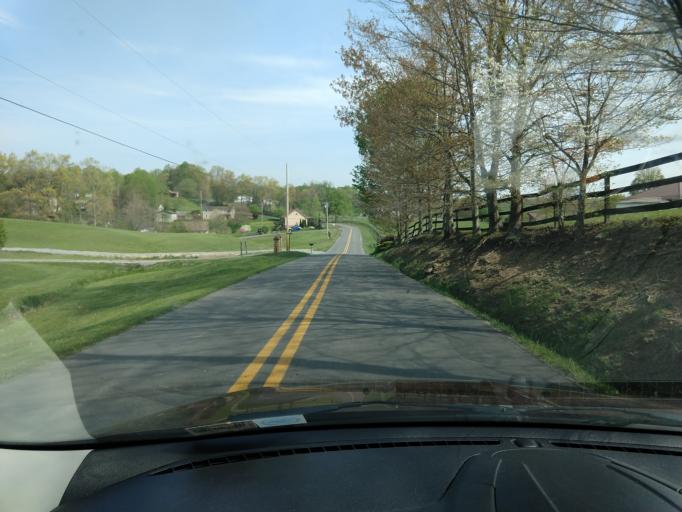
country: US
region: West Virginia
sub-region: Raleigh County
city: Crab Orchard
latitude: 37.7503
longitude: -81.2408
